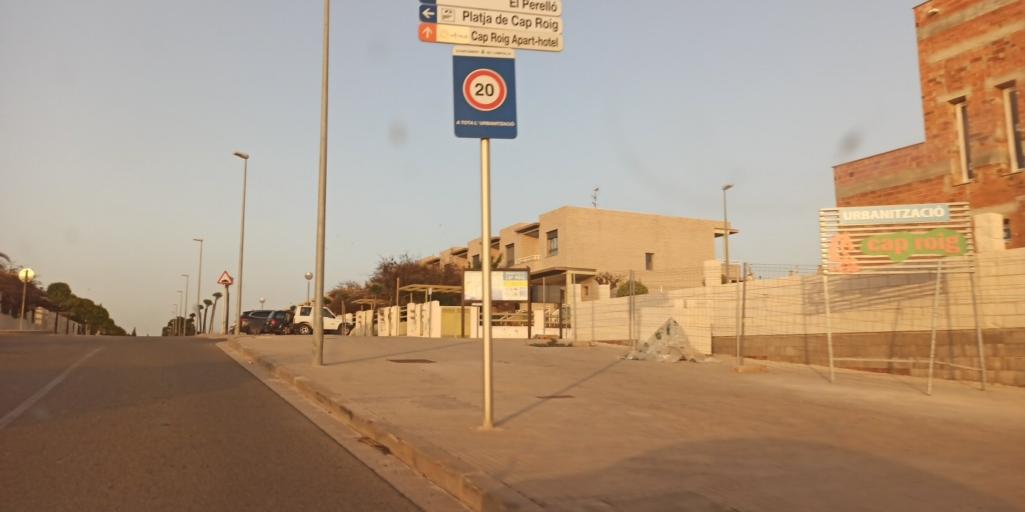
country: ES
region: Catalonia
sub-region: Provincia de Tarragona
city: L'Ampolla
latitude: 40.8210
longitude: 0.7261
